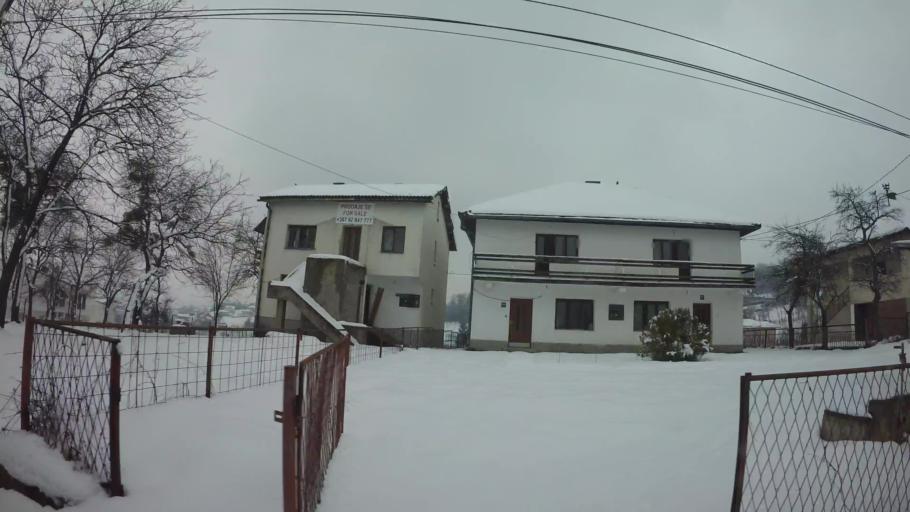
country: BA
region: Federation of Bosnia and Herzegovina
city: Hadzici
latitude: 43.8568
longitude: 18.2673
